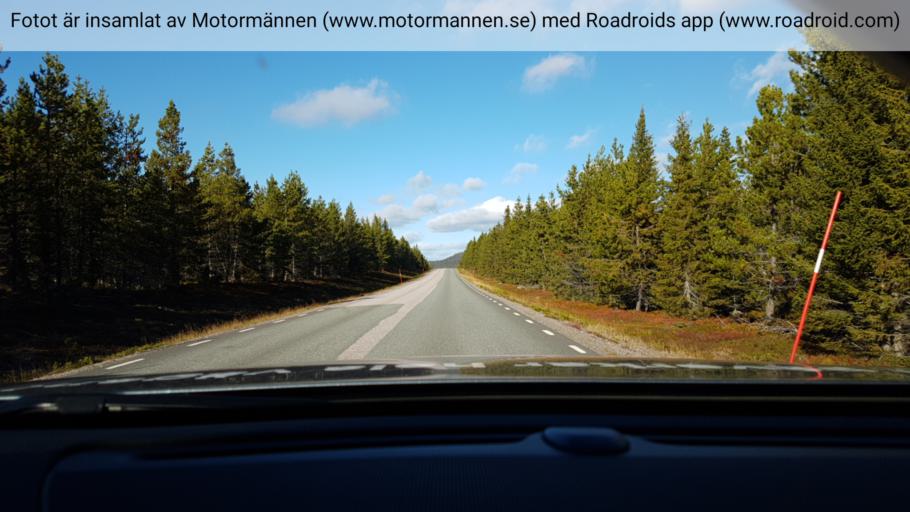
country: SE
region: Norrbotten
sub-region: Arjeplogs Kommun
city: Arjeplog
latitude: 65.8397
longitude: 18.4212
